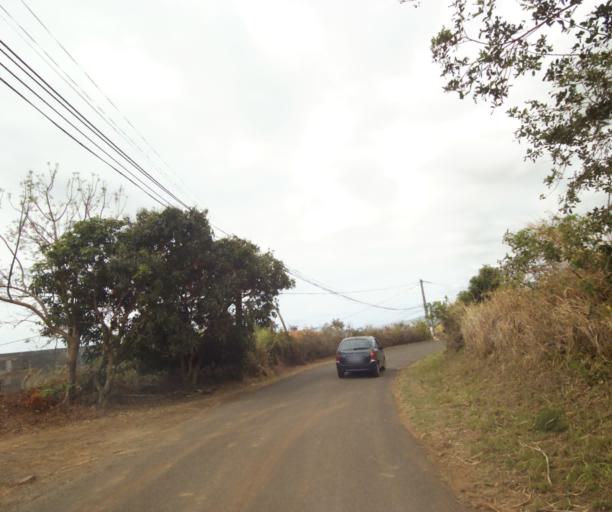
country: RE
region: Reunion
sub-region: Reunion
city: Saint-Paul
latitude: -21.0297
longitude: 55.2988
